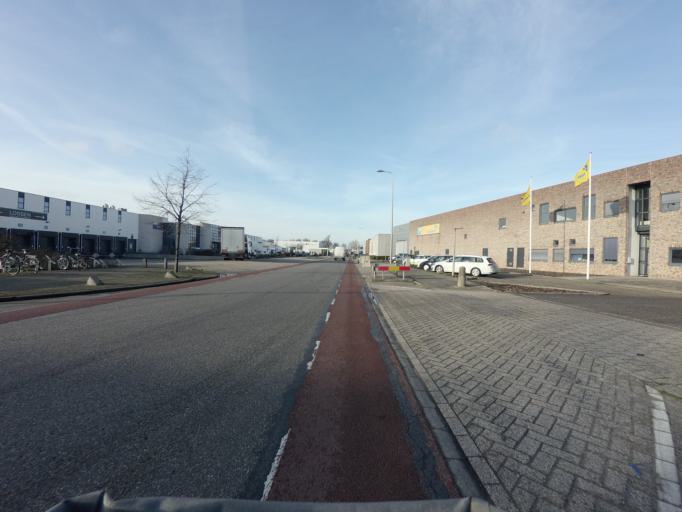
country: NL
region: Utrecht
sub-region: Stichtse Vecht
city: Maarssen
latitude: 52.1213
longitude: 5.0542
